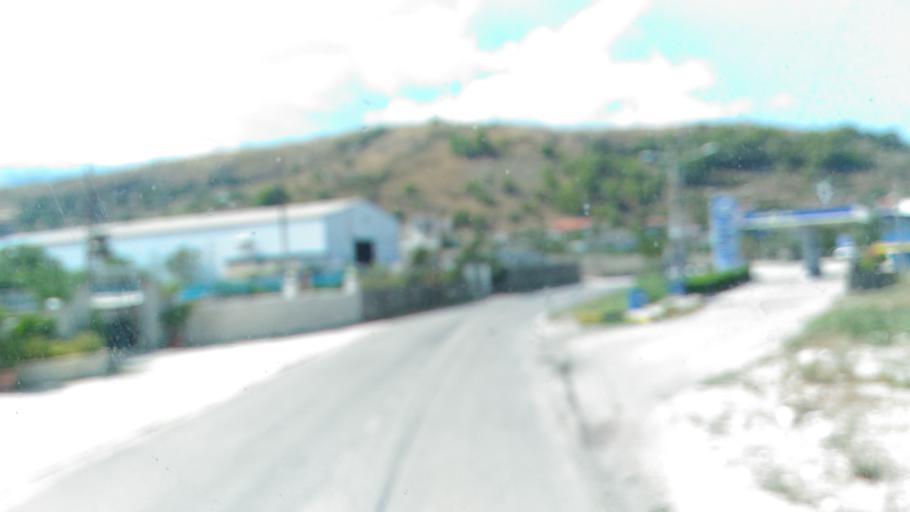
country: AL
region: Gjirokaster
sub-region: Rrethi i Gjirokastres
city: Dervician
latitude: 40.0567
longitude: 20.1734
